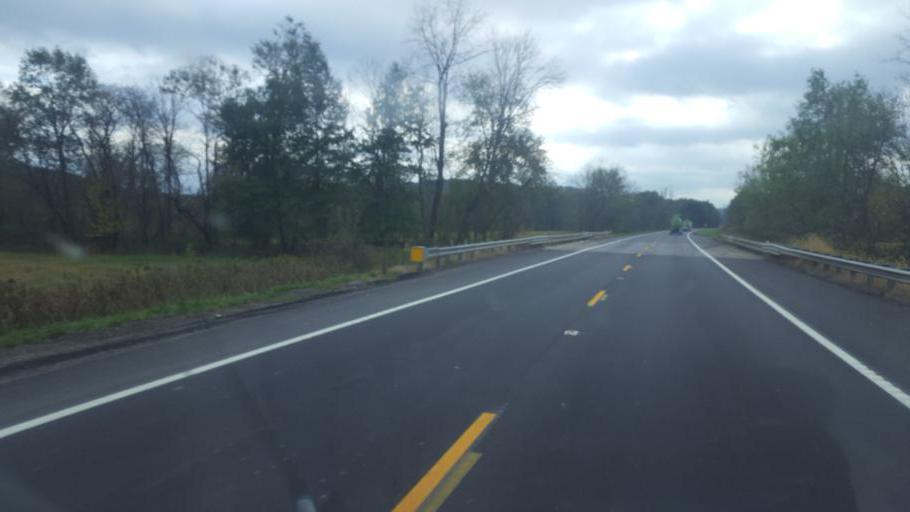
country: US
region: Ohio
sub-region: Tuscarawas County
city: Dennison
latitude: 40.3751
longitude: -81.2484
